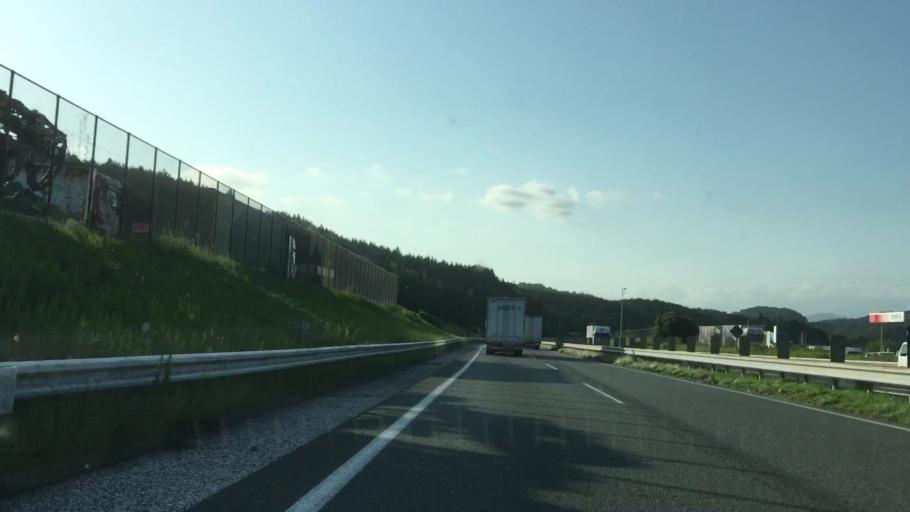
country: JP
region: Yamaguchi
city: Ogori-shimogo
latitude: 34.1532
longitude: 131.3383
